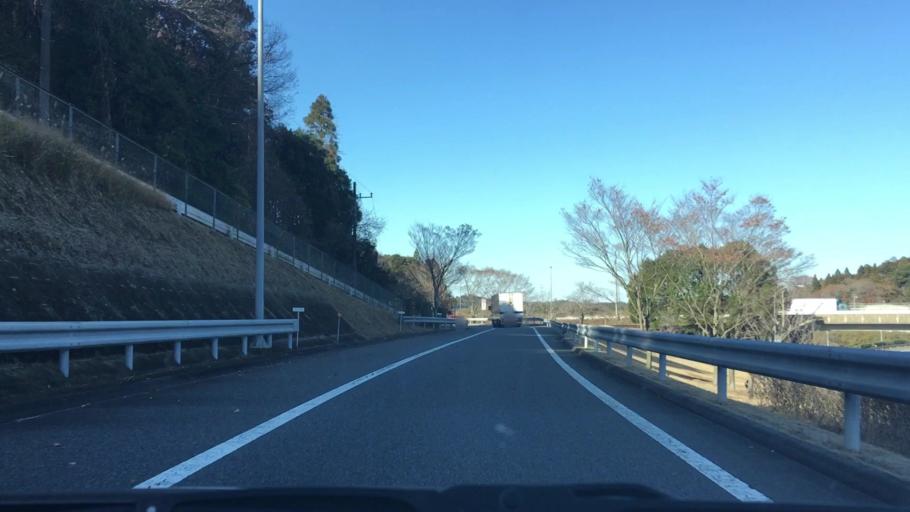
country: JP
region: Chiba
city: Sawara
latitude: 35.8421
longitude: 140.4444
